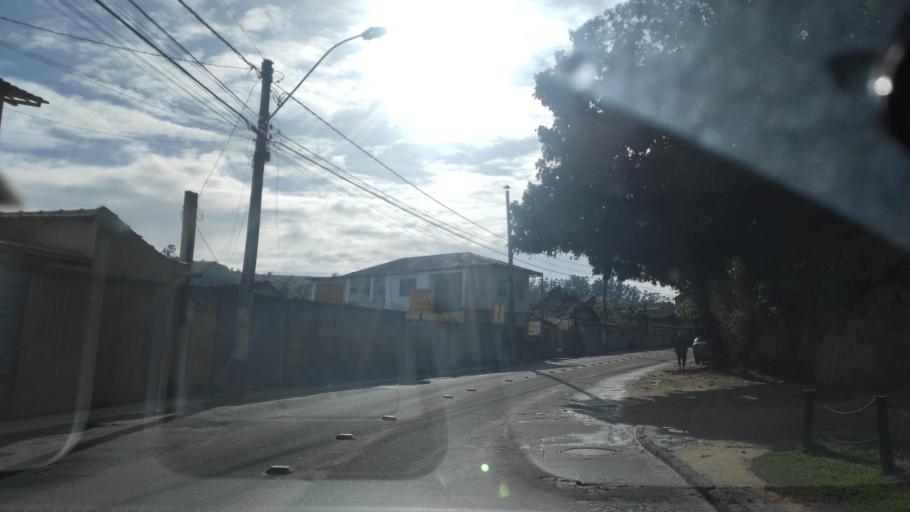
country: BR
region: Espirito Santo
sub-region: Nova Venecia
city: Nova Venecia
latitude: -18.7127
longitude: -40.3916
